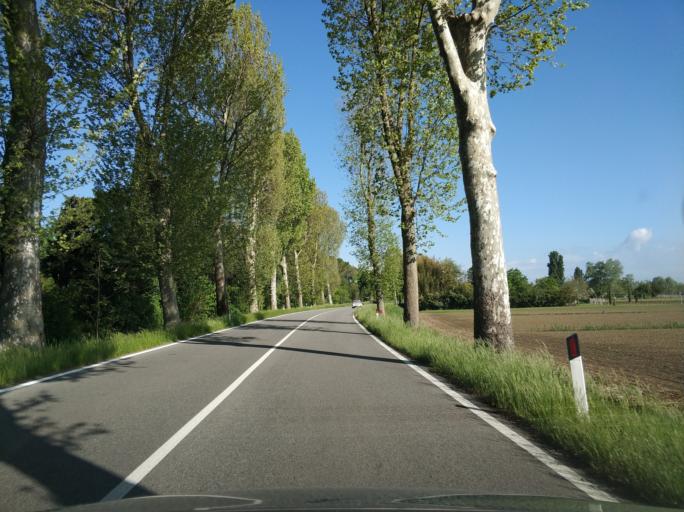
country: IT
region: Friuli Venezia Giulia
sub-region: Provincia di Udine
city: Terzo d'Aquileia
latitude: 45.8042
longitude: 13.3450
